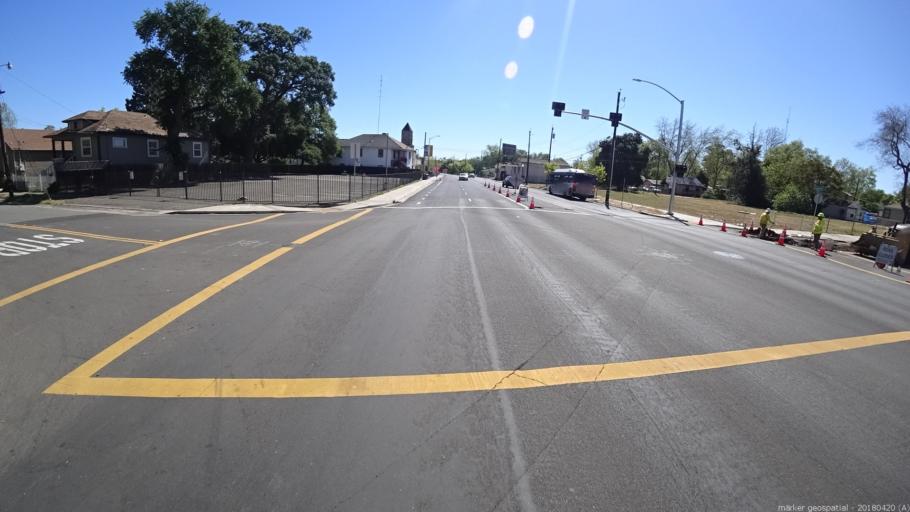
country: US
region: California
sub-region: Sacramento County
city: Sacramento
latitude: 38.5471
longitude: -121.4635
